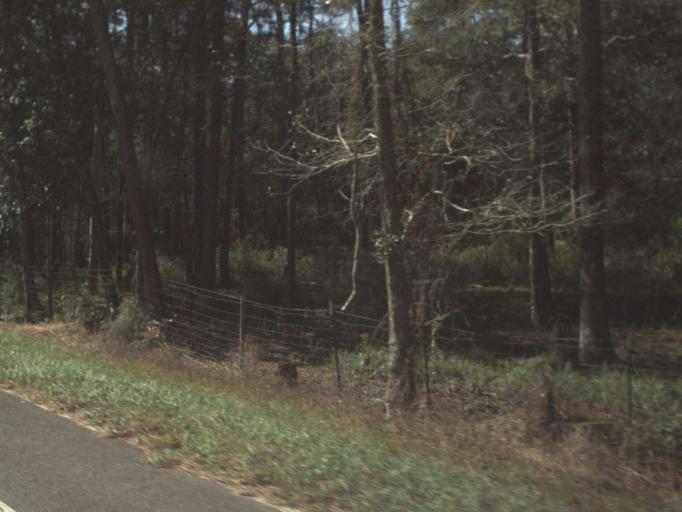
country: US
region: Alabama
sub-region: Geneva County
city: Samson
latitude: 30.9801
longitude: -86.1345
